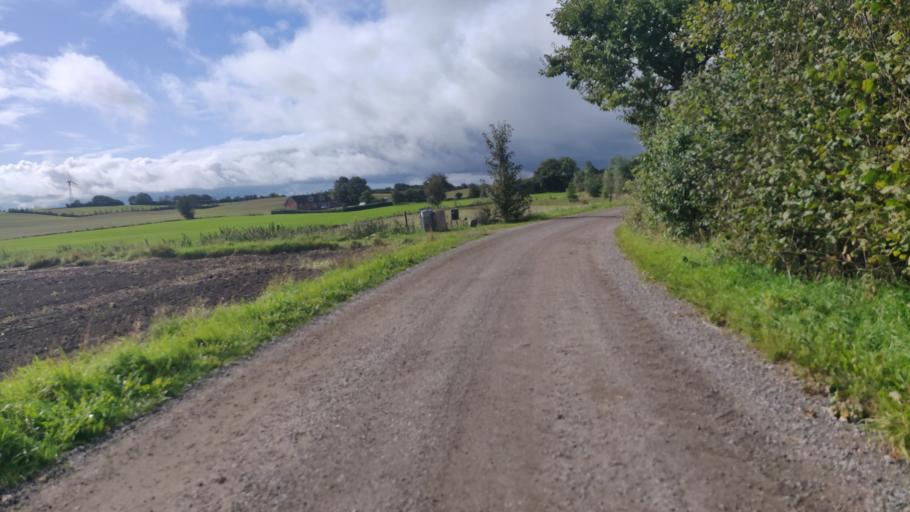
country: DK
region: South Denmark
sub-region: Kolding Kommune
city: Lunderskov
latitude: 55.5363
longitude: 9.3701
